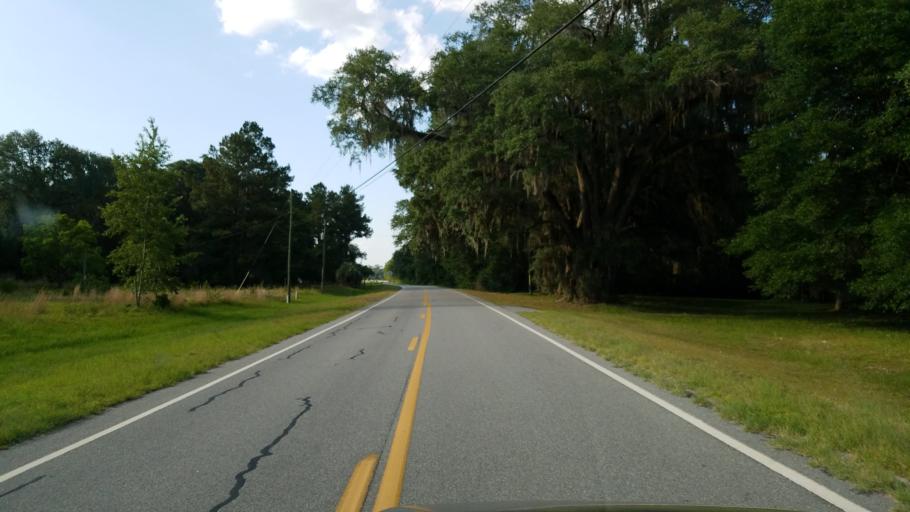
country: US
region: Georgia
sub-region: Echols County
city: Statenville
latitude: 30.7911
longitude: -83.0529
